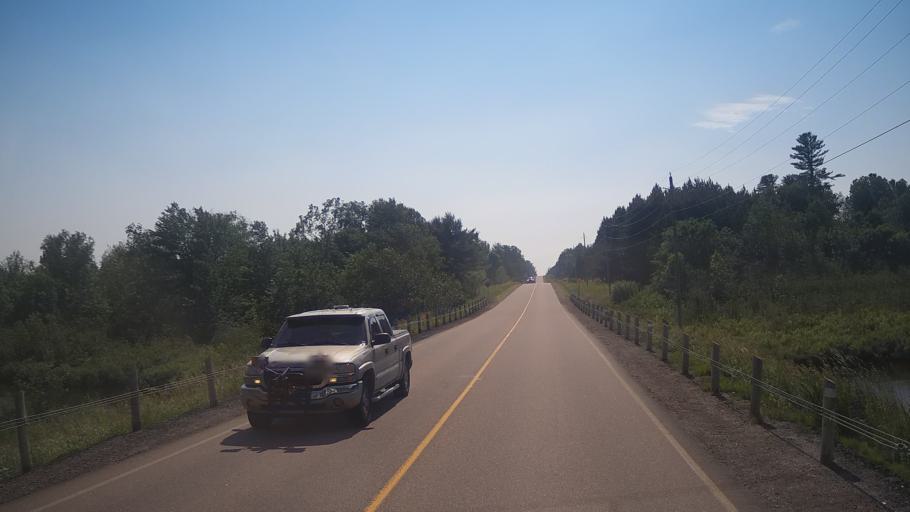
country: CA
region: Ontario
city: Pembroke
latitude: 45.6226
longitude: -77.1557
